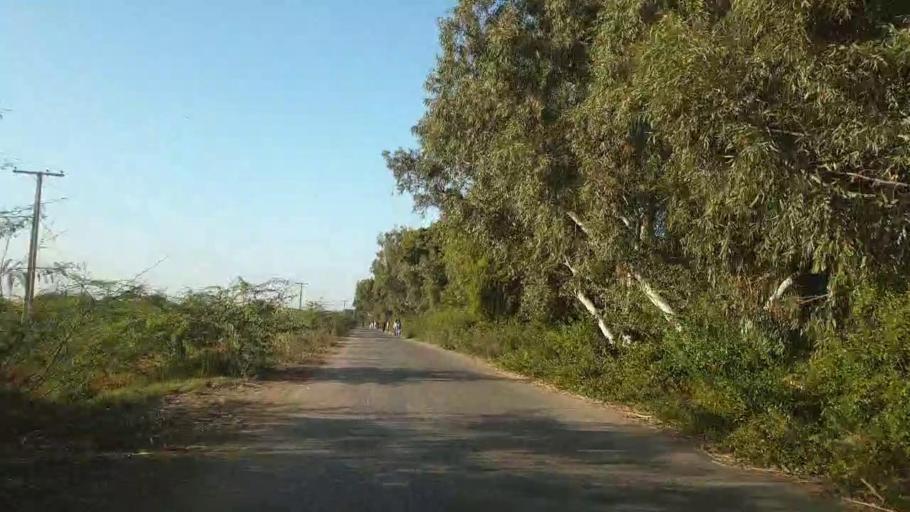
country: PK
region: Sindh
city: Mirpur Khas
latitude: 25.6534
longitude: 69.0976
